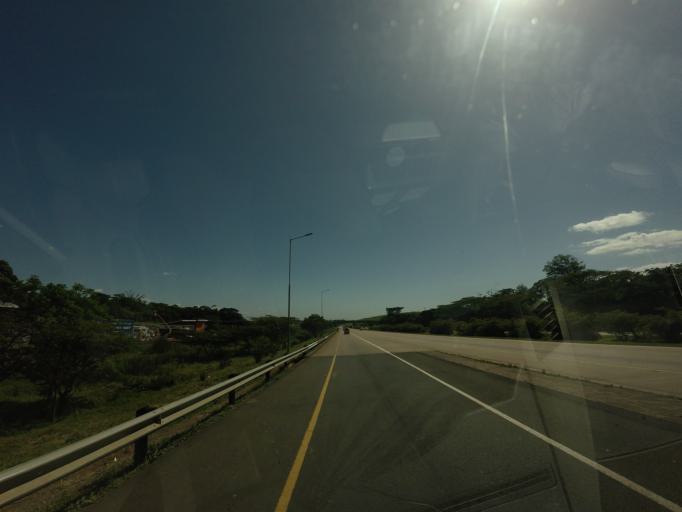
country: ZA
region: KwaZulu-Natal
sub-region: iLembe District Municipality
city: Ballitoville
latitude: -29.5130
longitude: 31.2024
